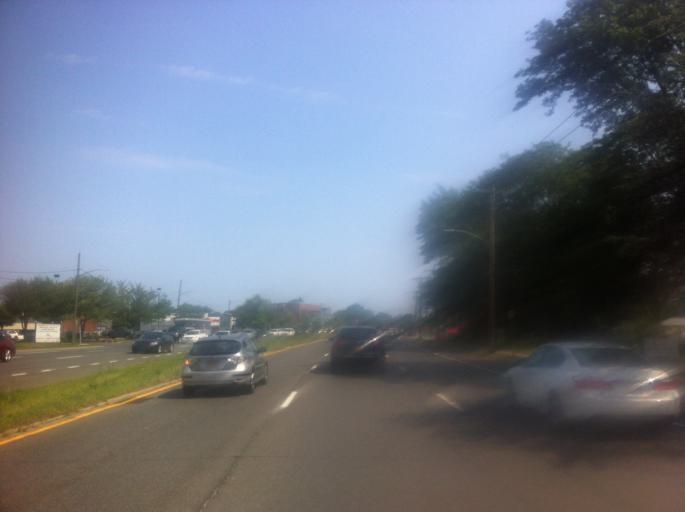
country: US
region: New York
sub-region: Nassau County
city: Jericho
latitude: 40.7897
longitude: -73.5370
